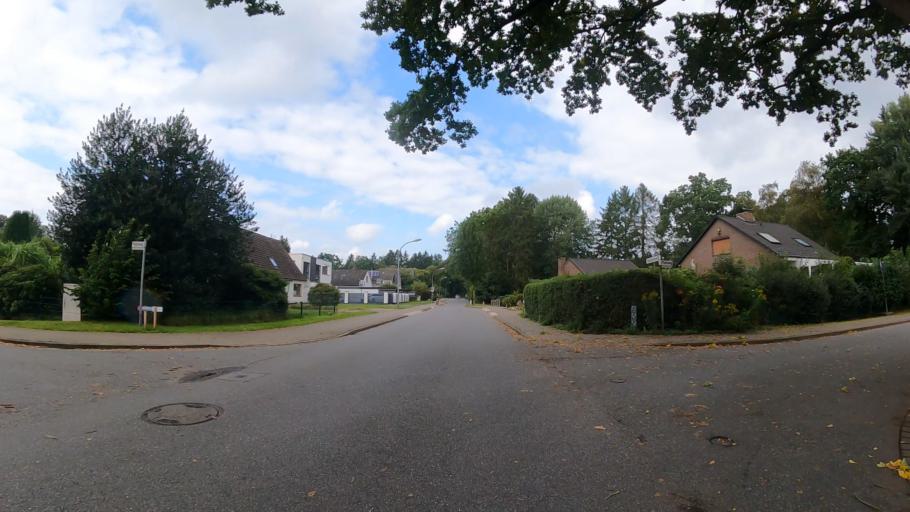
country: DE
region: Schleswig-Holstein
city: Tornesch
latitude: 53.7086
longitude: 9.7129
